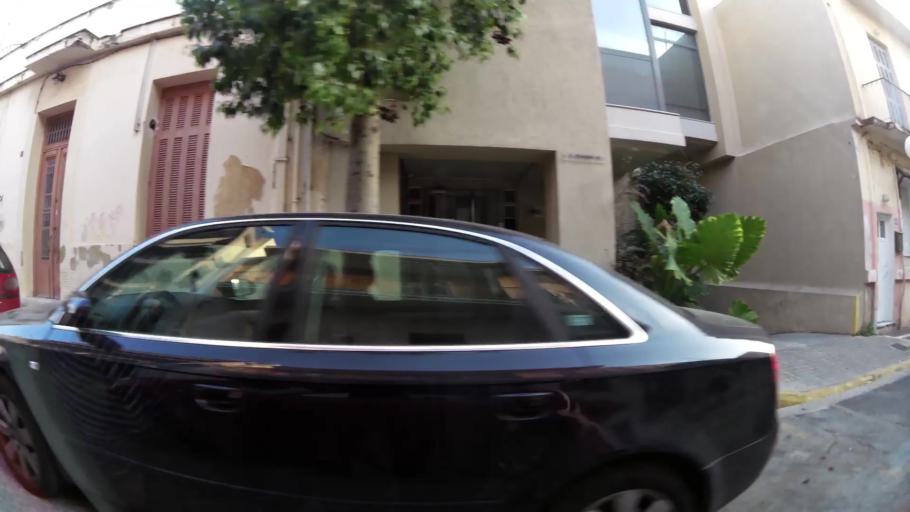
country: GR
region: Attica
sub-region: Nomarchia Athinas
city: Dhafni
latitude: 37.9558
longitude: 23.7394
